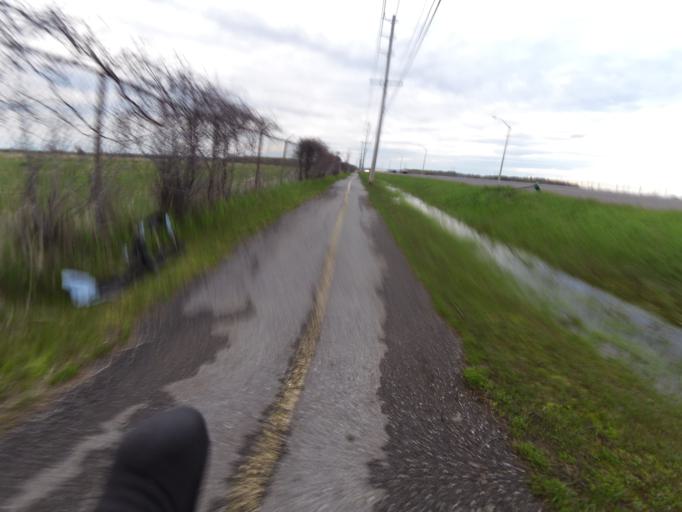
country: CA
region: Ontario
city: Bells Corners
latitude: 45.3023
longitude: -75.7657
